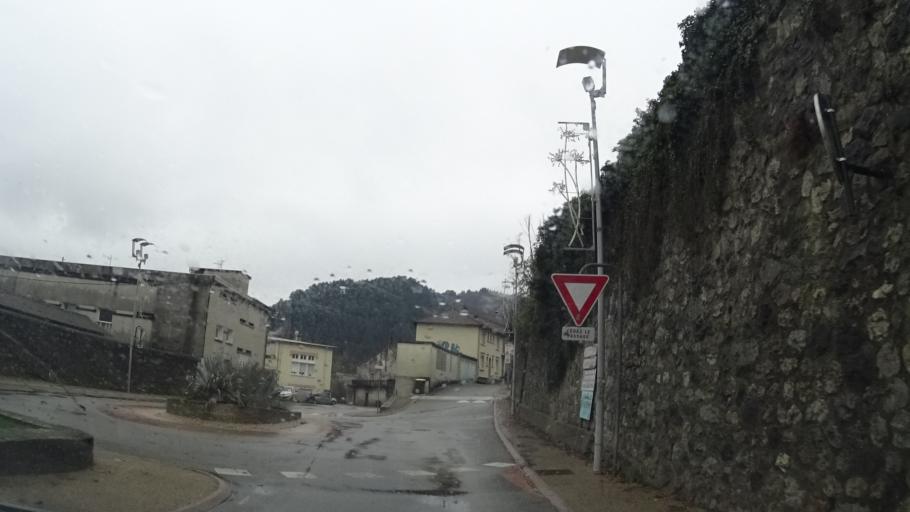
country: FR
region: Rhone-Alpes
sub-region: Departement de l'Ardeche
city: Labegude
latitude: 44.6532
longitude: 4.3652
